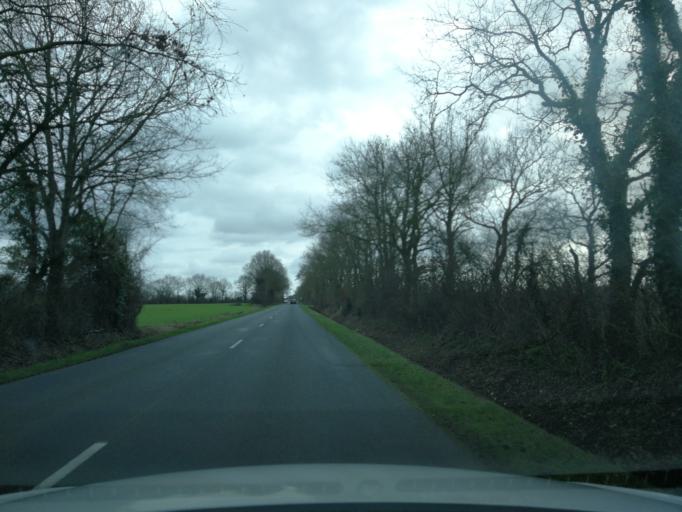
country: FR
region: Pays de la Loire
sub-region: Departement de la Loire-Atlantique
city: La Planche
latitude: 47.0071
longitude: -1.4744
